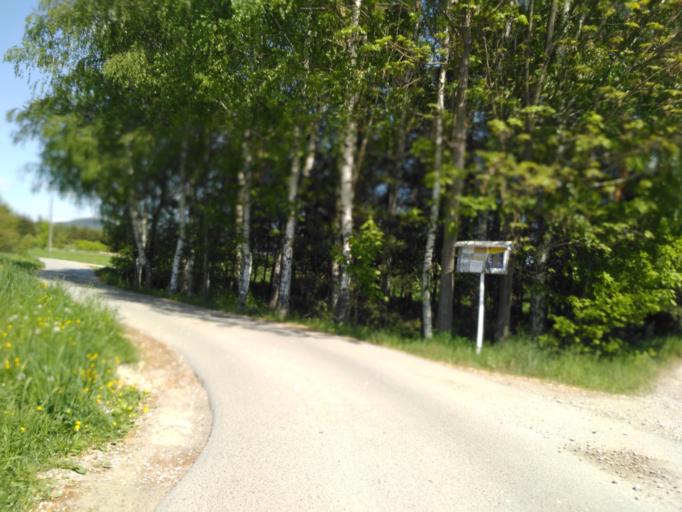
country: PL
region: Subcarpathian Voivodeship
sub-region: Powiat krosnienski
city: Odrzykon
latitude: 49.7256
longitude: 21.7301
